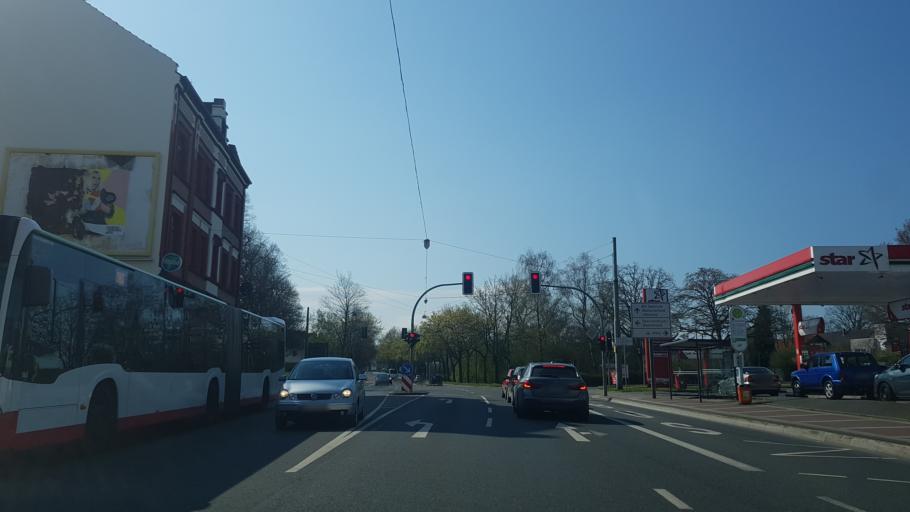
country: DE
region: North Rhine-Westphalia
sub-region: Regierungsbezirk Munster
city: Gelsenkirchen
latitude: 51.4724
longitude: 7.1451
